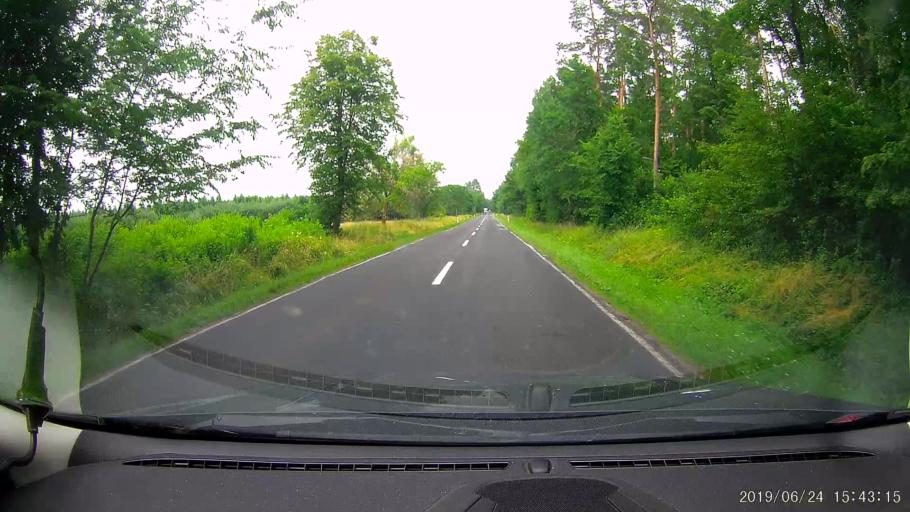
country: PL
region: Subcarpathian Voivodeship
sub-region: Powiat lubaczowski
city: Oleszyce
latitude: 50.1257
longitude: 22.9414
